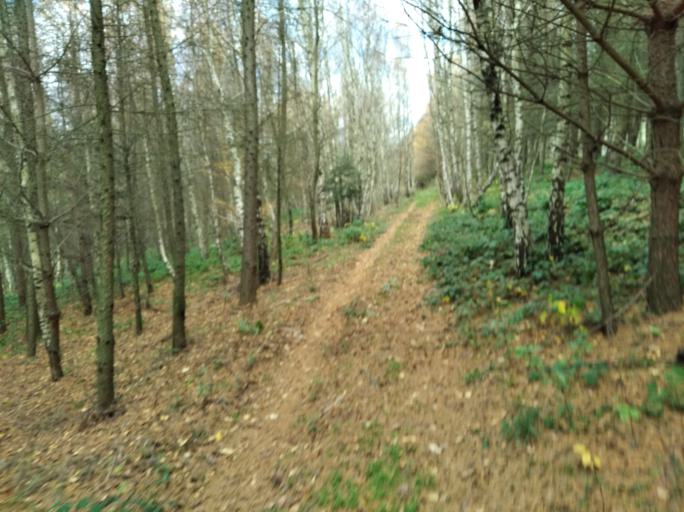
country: PL
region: Subcarpathian Voivodeship
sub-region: Powiat strzyzowski
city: Jawornik
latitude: 49.8563
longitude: 21.8517
